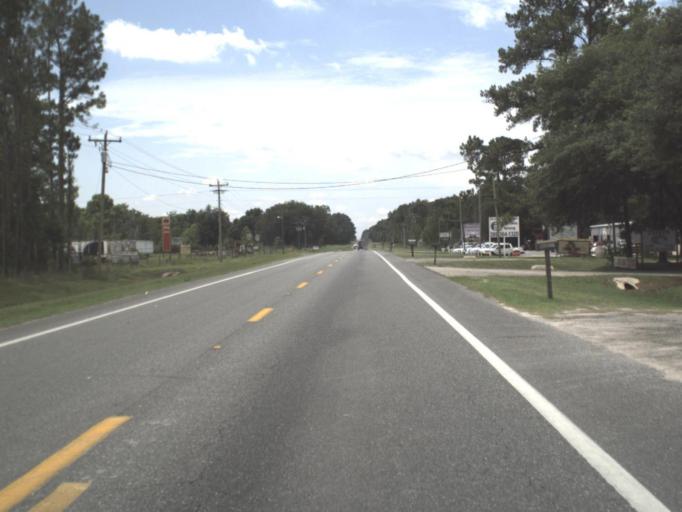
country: US
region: Florida
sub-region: Suwannee County
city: Live Oak
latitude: 30.2641
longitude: -82.9879
